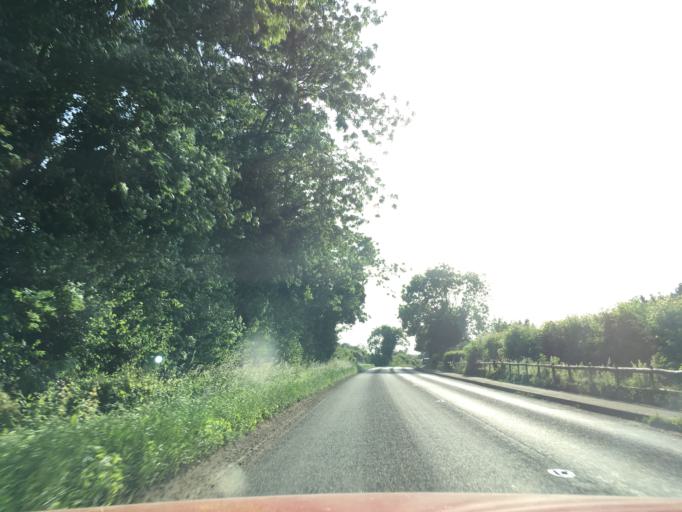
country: GB
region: England
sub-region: Gloucestershire
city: Fairford
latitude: 51.7014
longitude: -1.8342
